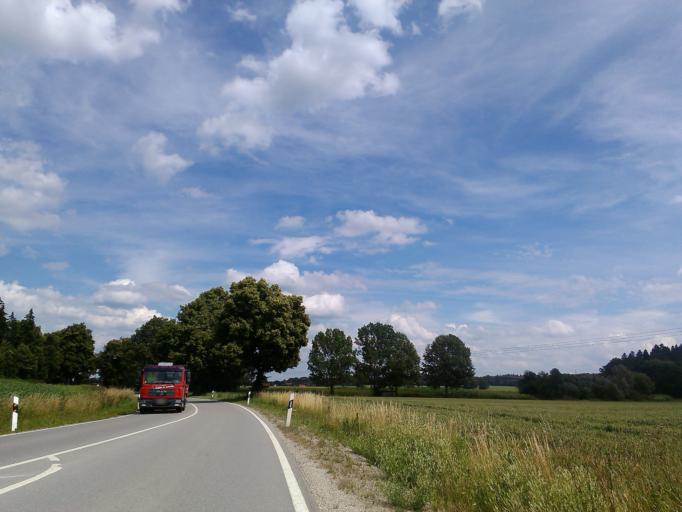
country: DE
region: Bavaria
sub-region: Upper Bavaria
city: Gilching
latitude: 48.0663
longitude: 11.3096
